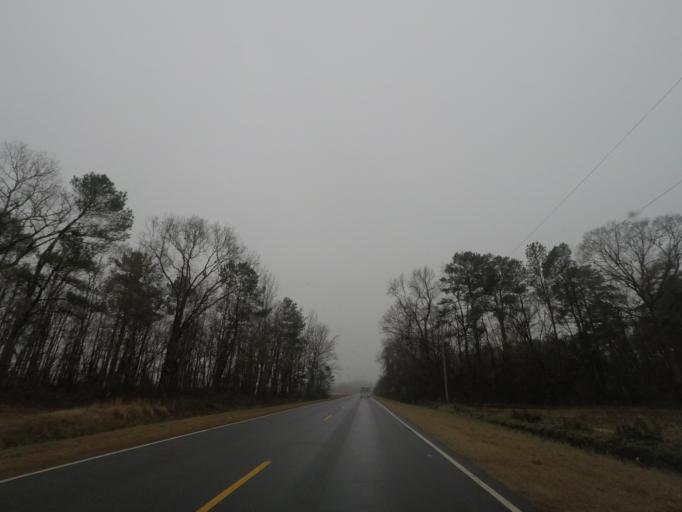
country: US
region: North Carolina
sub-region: Scotland County
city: Laurinburg
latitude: 34.7849
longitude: -79.4304
